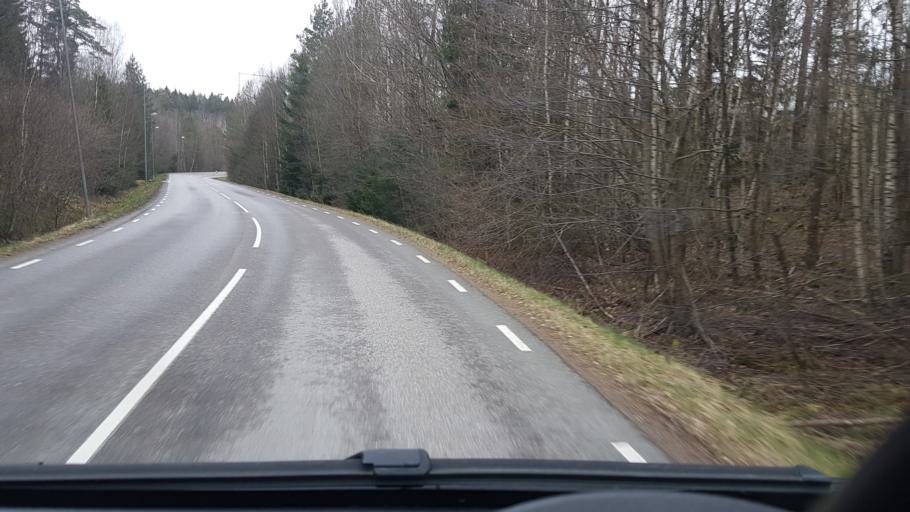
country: SE
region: Vaestra Goetaland
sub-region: Lerums Kommun
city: Stenkullen
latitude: 57.8067
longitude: 12.3348
